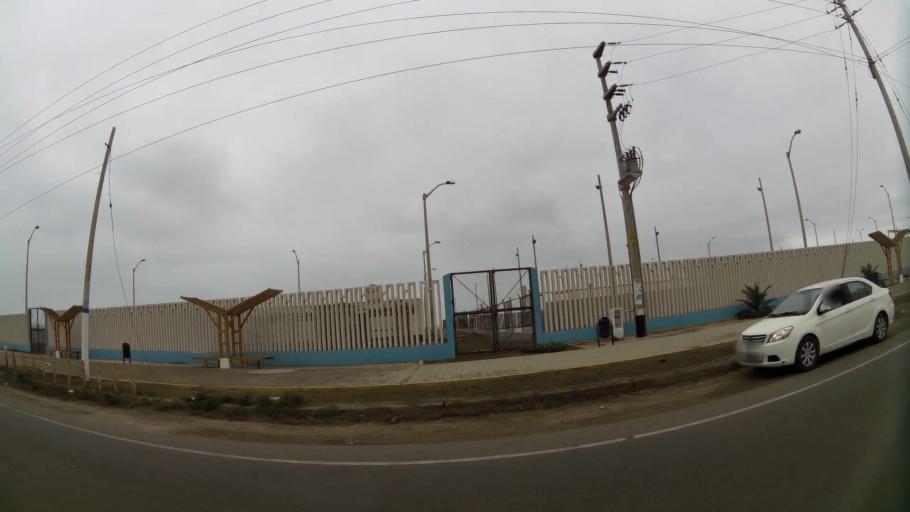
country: PE
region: Ica
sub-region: Provincia de Pisco
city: Pisco
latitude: -13.7178
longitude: -76.2198
